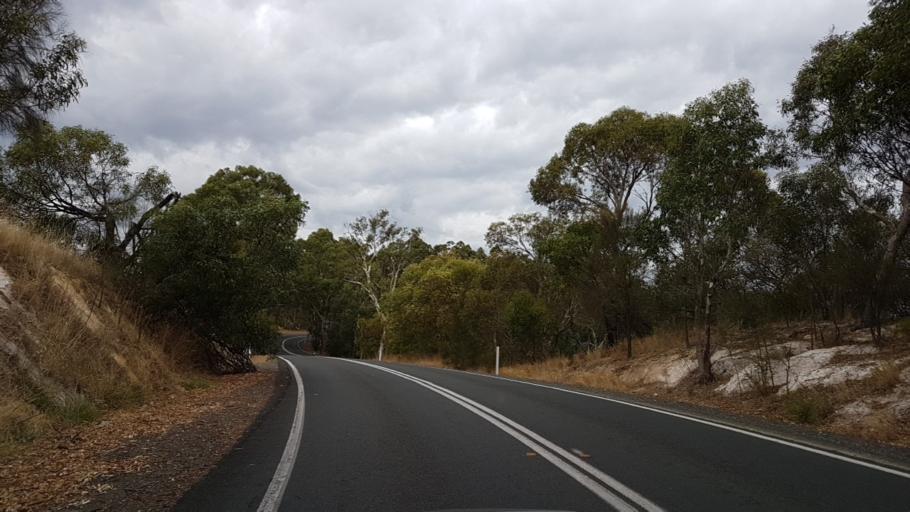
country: AU
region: South Australia
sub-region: Adelaide Hills
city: Gumeracha
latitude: -34.7793
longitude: 138.8940
